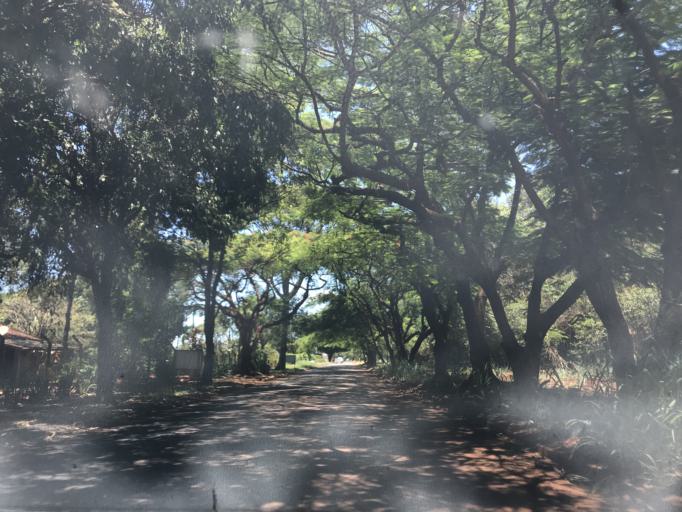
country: BR
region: Parana
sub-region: Sarandi
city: Sarandi
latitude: -23.4428
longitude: -51.9060
